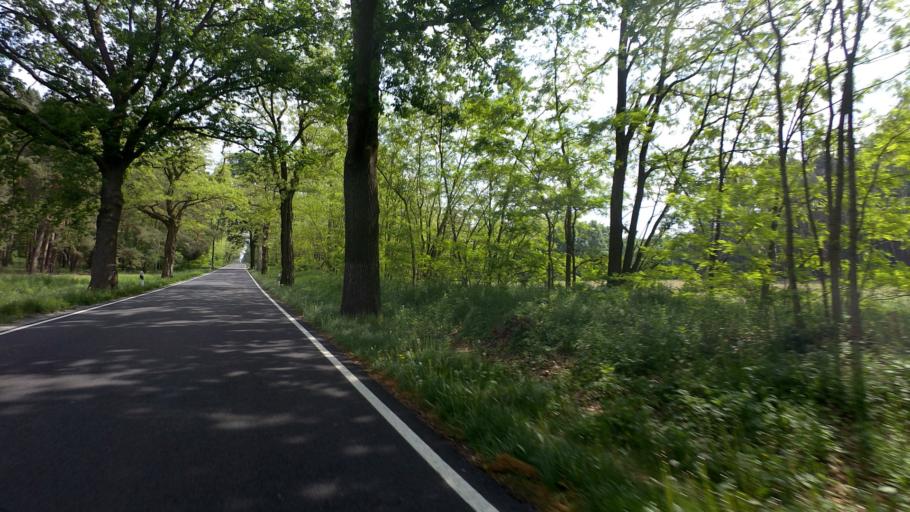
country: DE
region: Brandenburg
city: Neu Zauche
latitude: 52.0027
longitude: 14.1473
